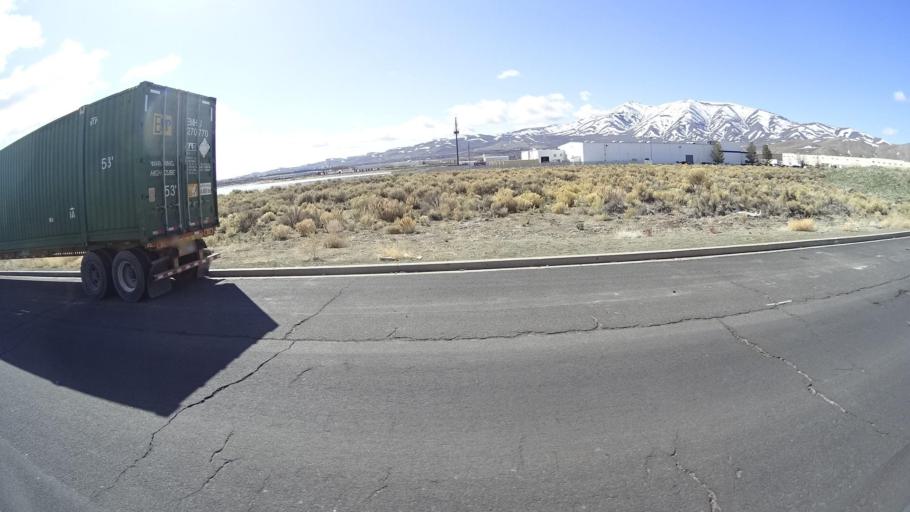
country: US
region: Nevada
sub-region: Washoe County
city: Lemmon Valley
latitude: 39.6547
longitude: -119.8949
